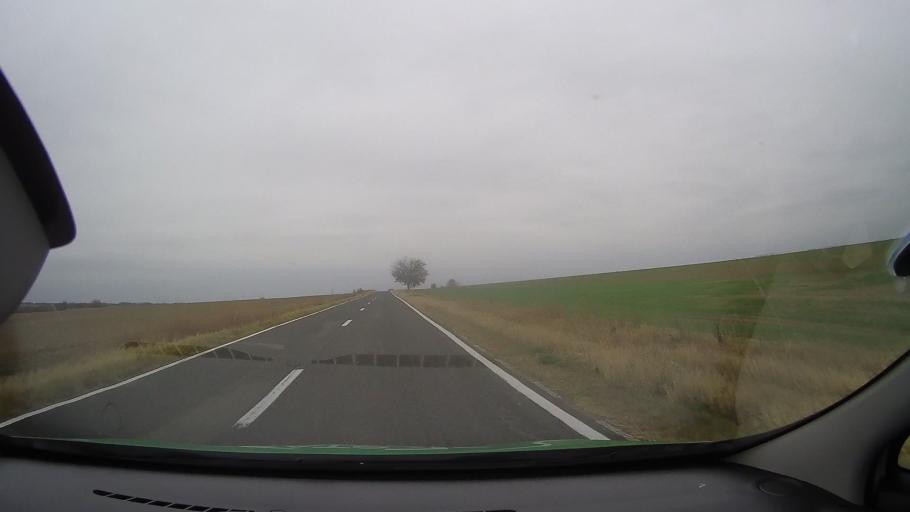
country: RO
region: Constanta
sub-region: Comuna Garliciu
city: Garliciu
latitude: 44.7107
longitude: 28.0900
